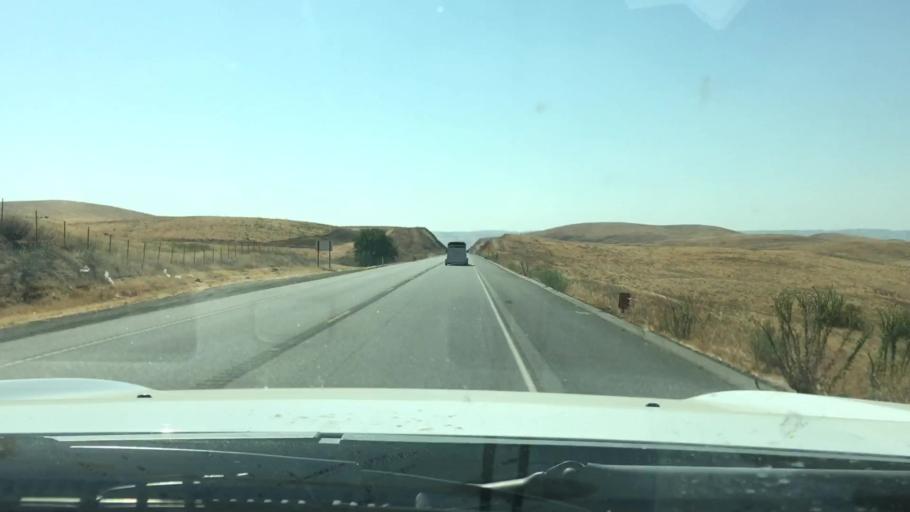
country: US
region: California
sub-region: San Luis Obispo County
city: Shandon
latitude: 35.7434
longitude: -120.2288
